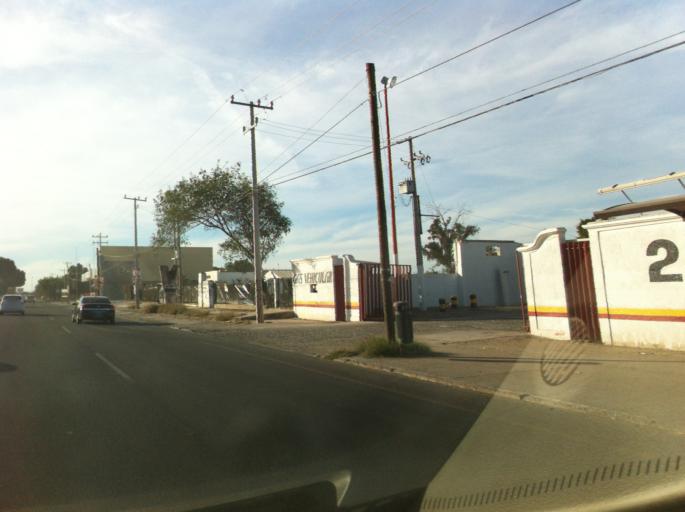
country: MX
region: Sonora
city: Hermosillo
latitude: 29.0948
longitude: -111.0096
